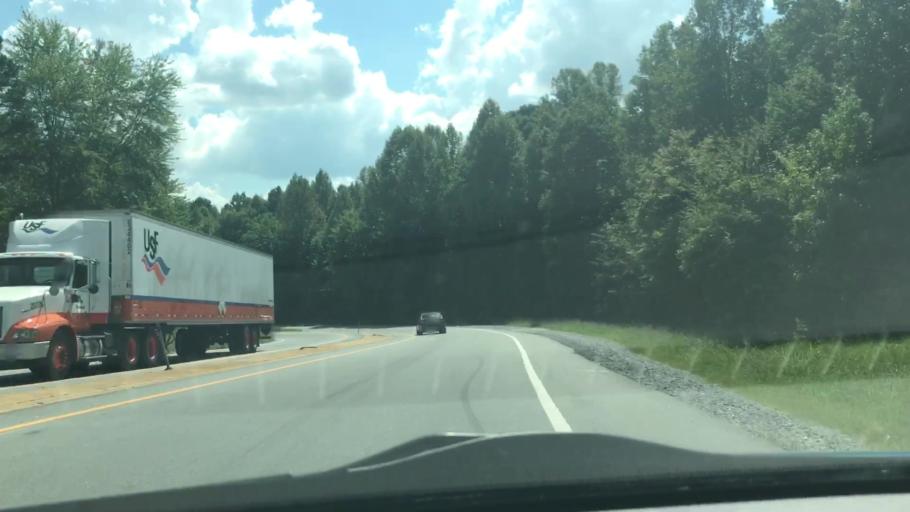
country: US
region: North Carolina
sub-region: Randolph County
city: Randleman
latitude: 35.8027
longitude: -79.8235
